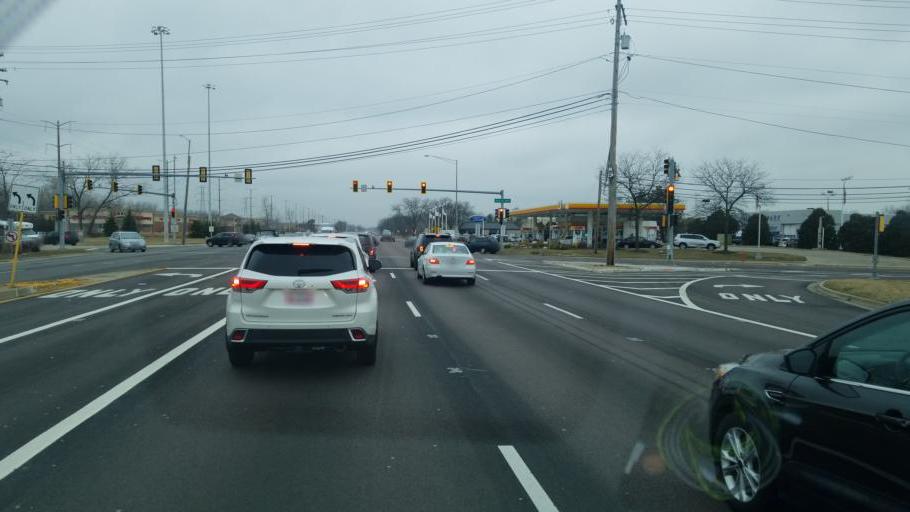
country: US
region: Illinois
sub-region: Lake County
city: Highwood
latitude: 42.1886
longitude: -87.8251
